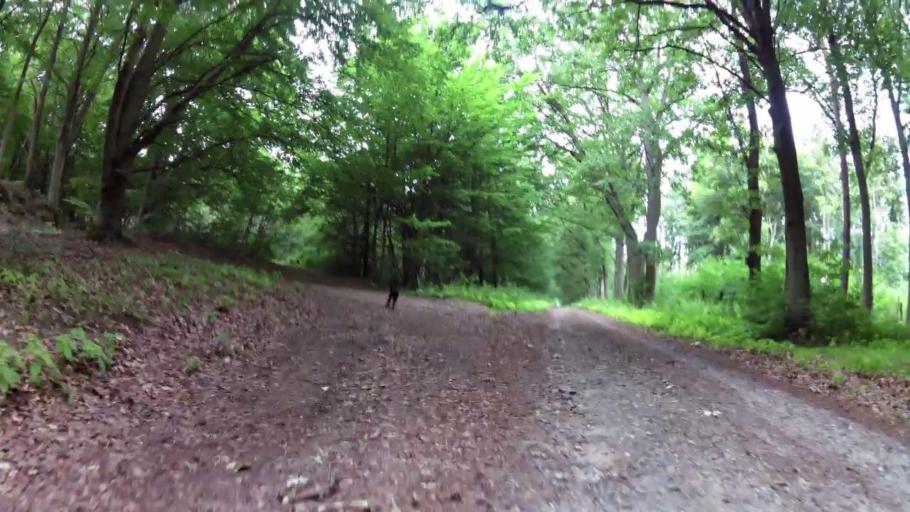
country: PL
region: West Pomeranian Voivodeship
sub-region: Powiat lobeski
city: Lobez
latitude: 53.7528
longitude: 15.5995
